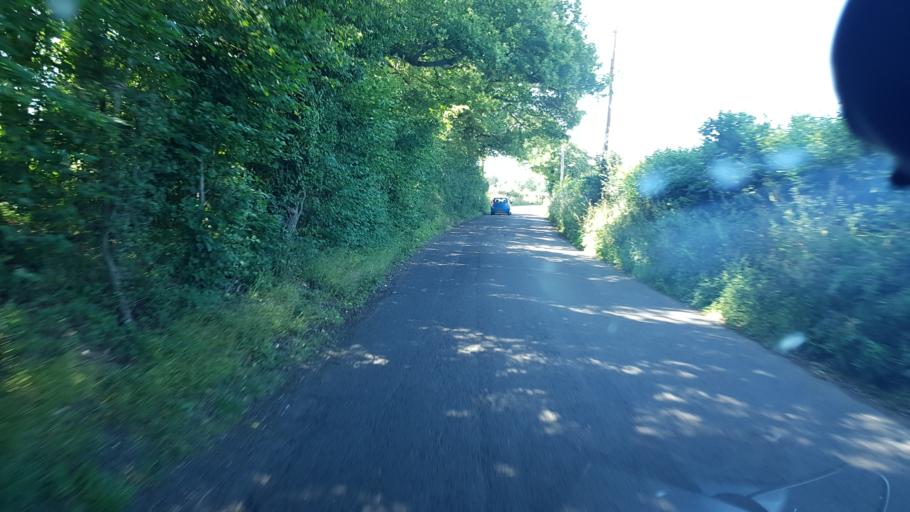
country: GB
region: England
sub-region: Kent
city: Edenbridge
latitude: 51.2255
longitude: 0.0755
